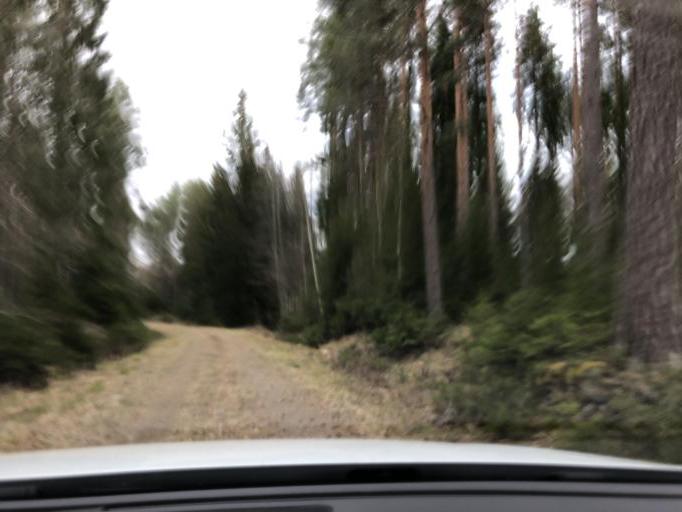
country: SE
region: Gaevleborg
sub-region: Gavle Kommun
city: Hedesunda
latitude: 60.3373
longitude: 17.0627
